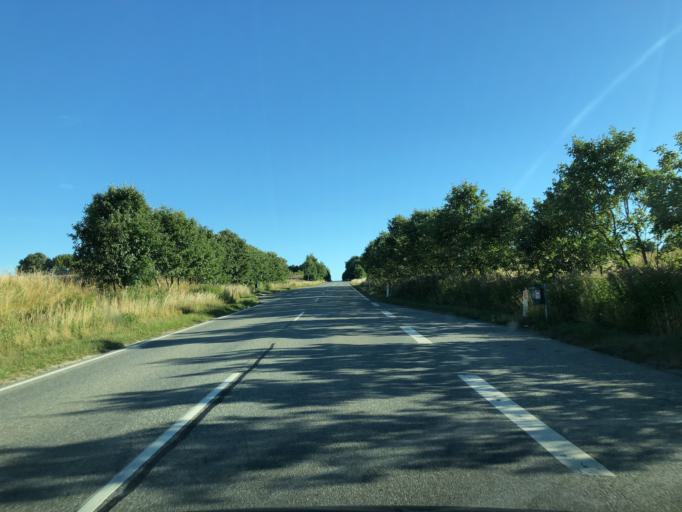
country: DK
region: Central Jutland
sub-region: Arhus Kommune
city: Framlev
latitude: 56.1216
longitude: 9.9903
